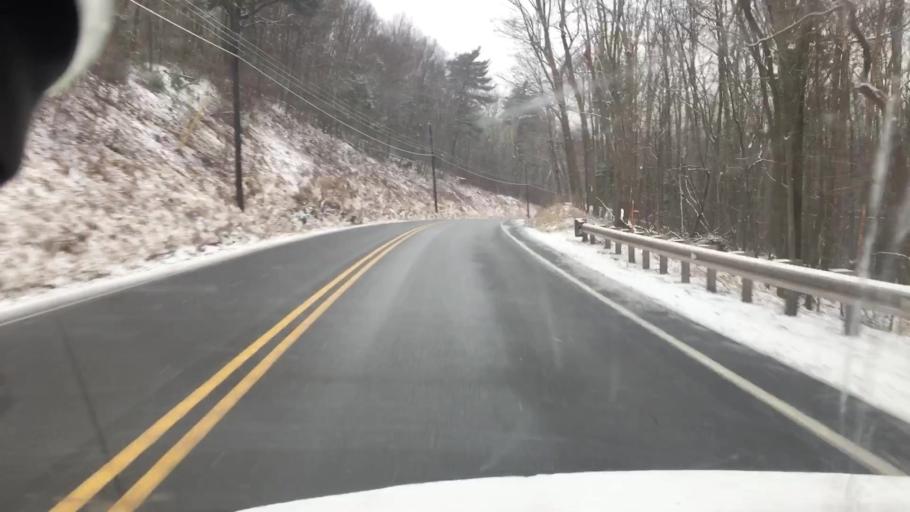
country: US
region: Pennsylvania
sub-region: Luzerne County
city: Conyngham
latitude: 41.0320
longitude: -76.1240
